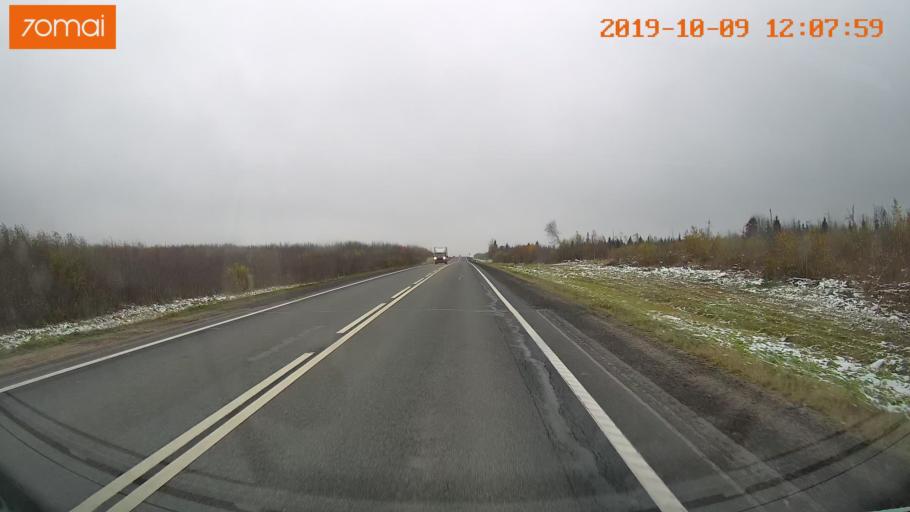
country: RU
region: Jaroslavl
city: Prechistoye
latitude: 58.5926
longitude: 40.3452
